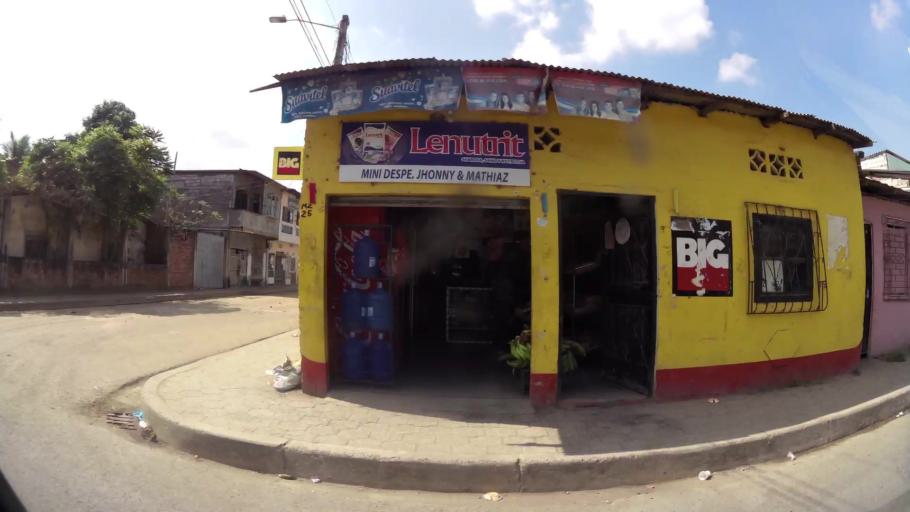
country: EC
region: Guayas
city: Eloy Alfaro
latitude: -2.1689
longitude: -79.8260
